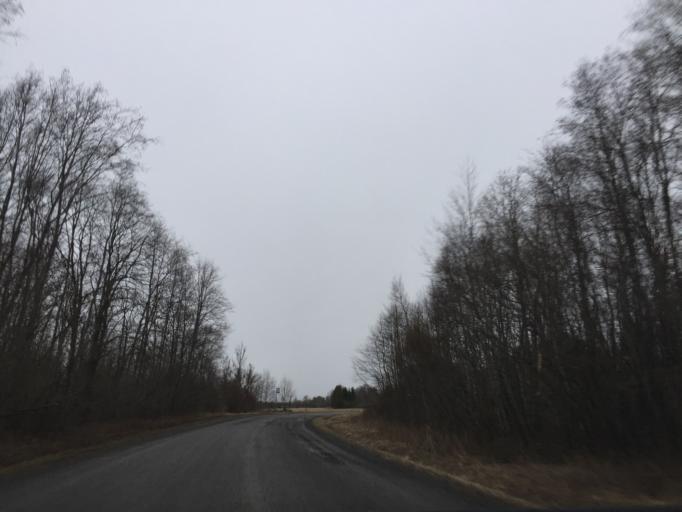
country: EE
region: Laeaene
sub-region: Lihula vald
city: Lihula
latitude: 58.6343
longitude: 23.6300
